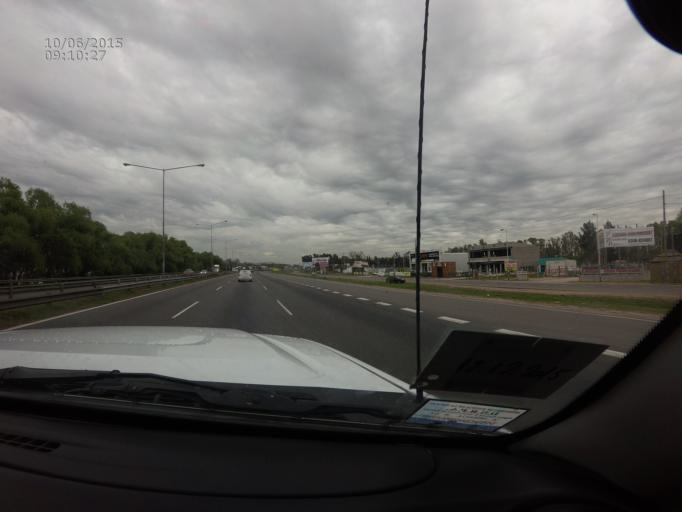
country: AR
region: Buenos Aires
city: Belen de Escobar
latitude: -34.3701
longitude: -58.7723
